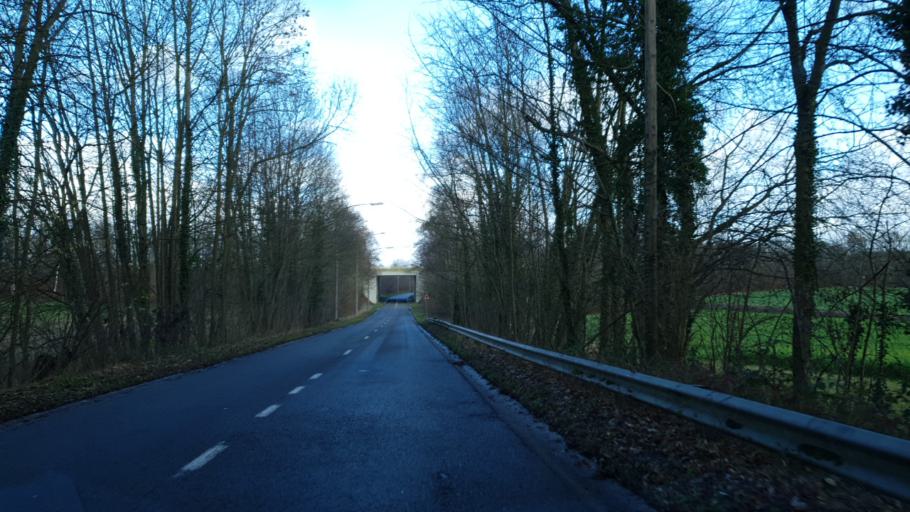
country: BE
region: Flanders
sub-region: Provincie Vlaams-Brabant
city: Kortenberg
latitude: 50.8667
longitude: 4.5603
